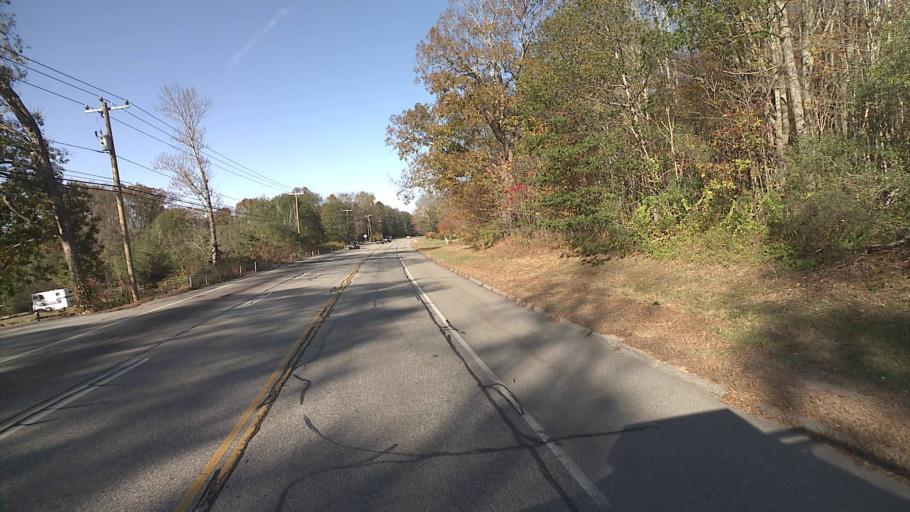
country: US
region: Connecticut
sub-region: Windham County
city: Windham
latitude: 41.7676
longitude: -72.1152
